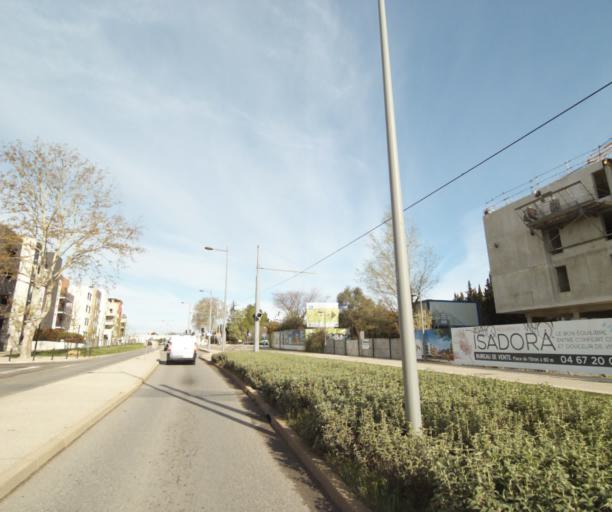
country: FR
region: Languedoc-Roussillon
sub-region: Departement de l'Herault
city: Saint-Jean-de-Vedas
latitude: 43.5742
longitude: 3.8319
